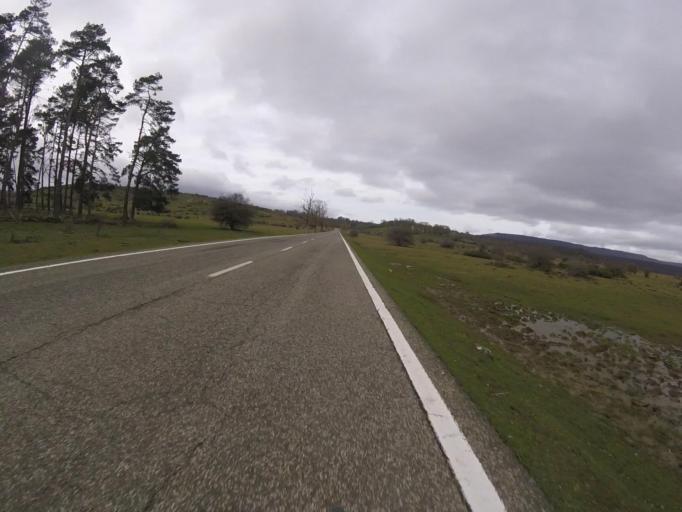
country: ES
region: Navarre
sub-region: Provincia de Navarra
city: Eulate
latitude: 42.8127
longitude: -2.1619
